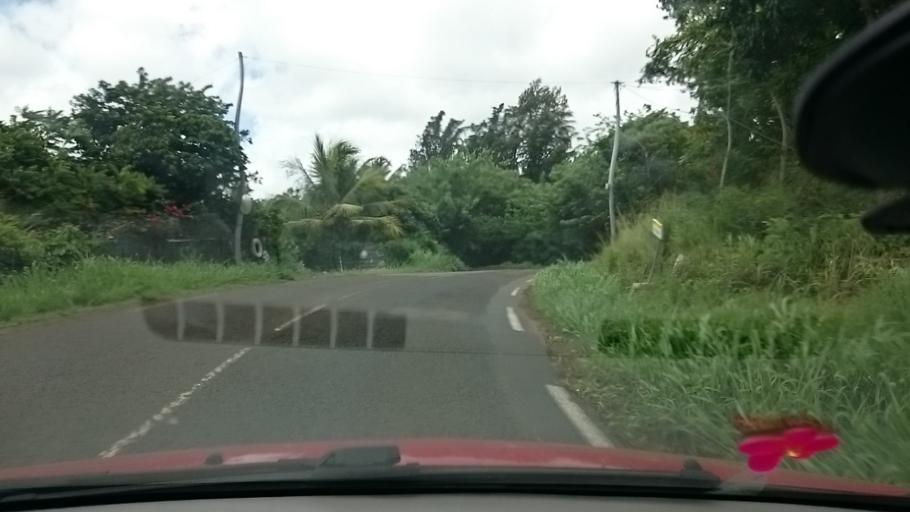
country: MQ
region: Martinique
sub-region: Martinique
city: Le Francois
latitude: 14.5856
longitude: -60.9238
